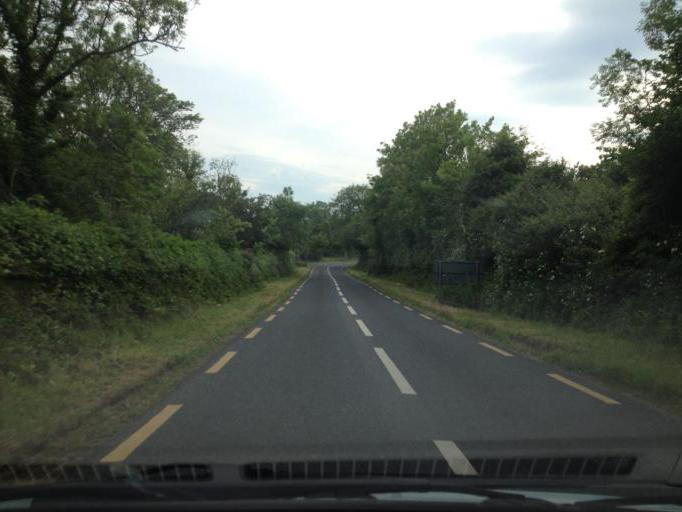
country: IE
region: Connaught
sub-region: Sligo
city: Sligo
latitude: 54.2788
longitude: -8.4425
